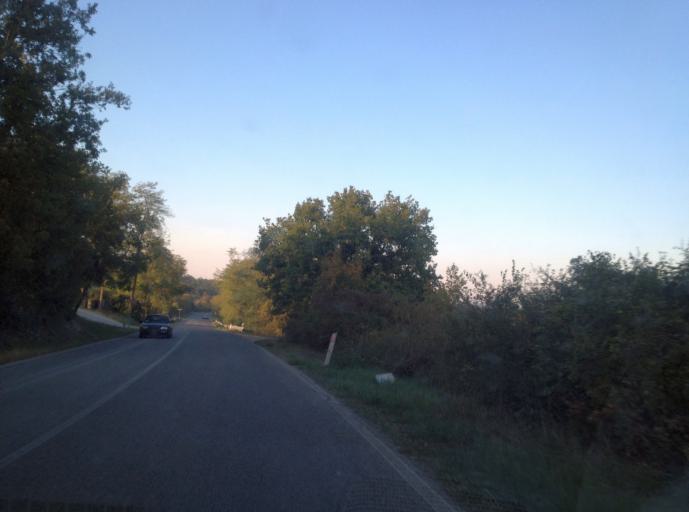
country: IT
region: Tuscany
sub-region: Provincia di Siena
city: Castellina in Chianti
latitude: 43.4786
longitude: 11.2979
